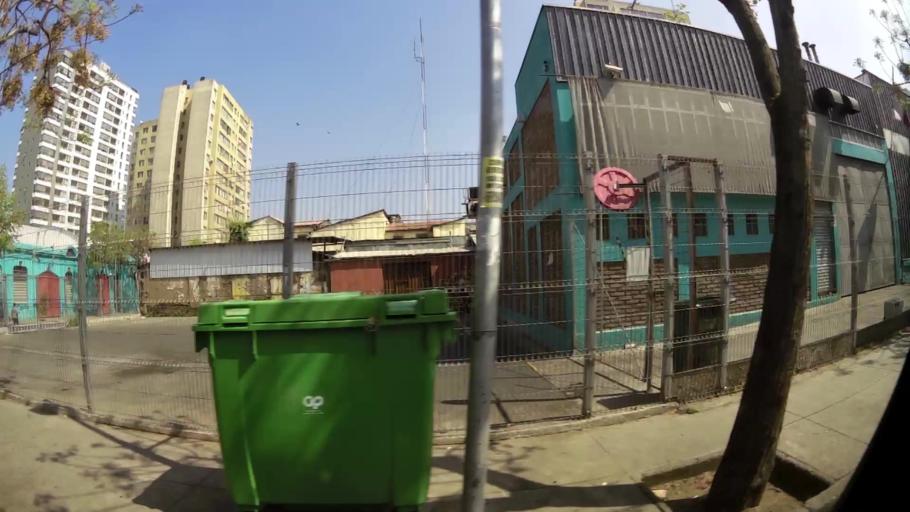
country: CL
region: Santiago Metropolitan
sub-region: Provincia de Santiago
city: Santiago
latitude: -33.4574
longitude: -70.6548
